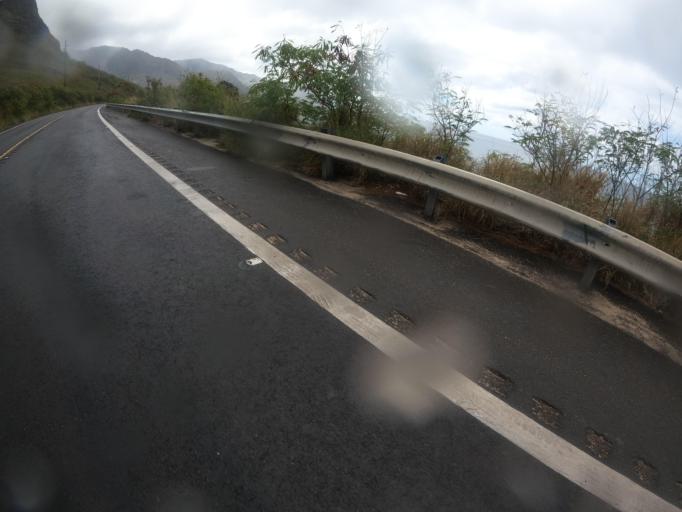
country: US
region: Hawaii
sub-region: Honolulu County
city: Makaha Valley
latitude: 21.5447
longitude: -158.2390
